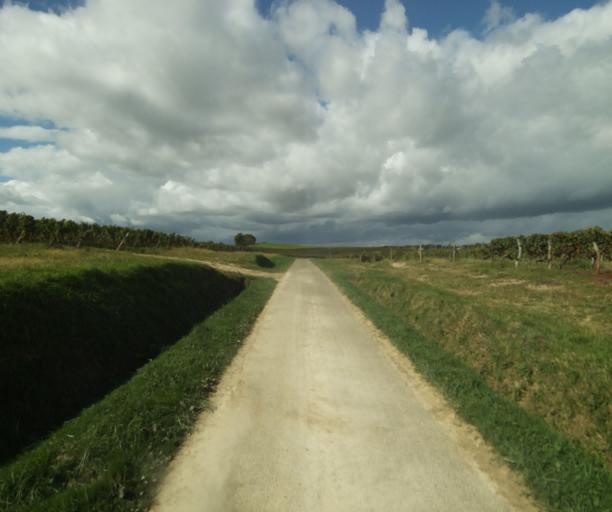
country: FR
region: Midi-Pyrenees
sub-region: Departement du Gers
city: Nogaro
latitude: 43.8480
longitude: -0.0315
